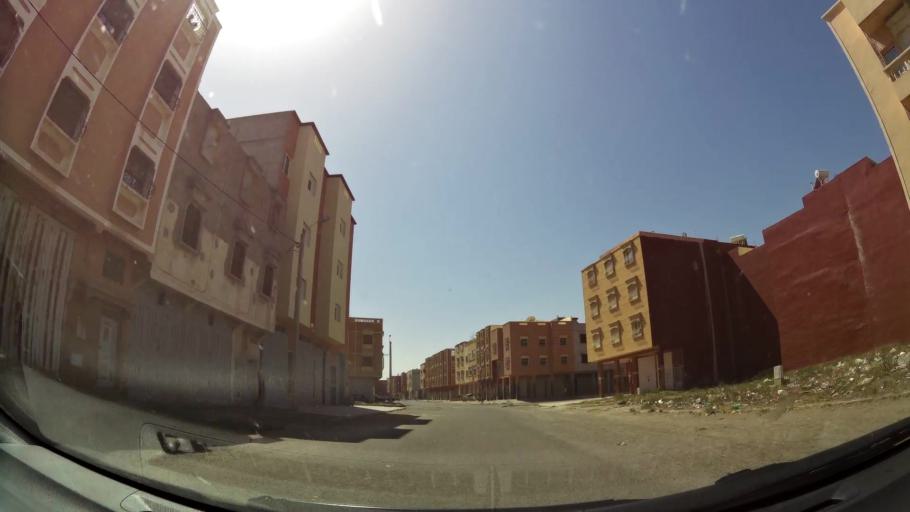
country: MA
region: Souss-Massa-Draa
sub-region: Inezgane-Ait Mellou
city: Inezgane
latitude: 30.3317
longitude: -9.5089
